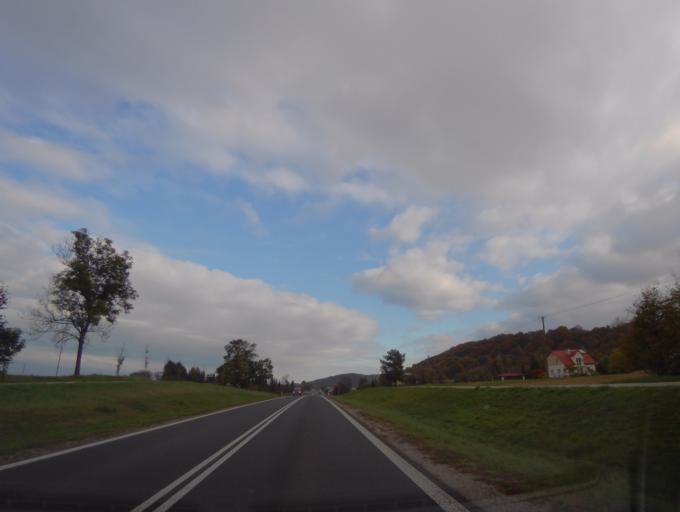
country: PL
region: Lublin Voivodeship
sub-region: Powiat bilgorajski
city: Goraj
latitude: 50.7417
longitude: 22.6694
